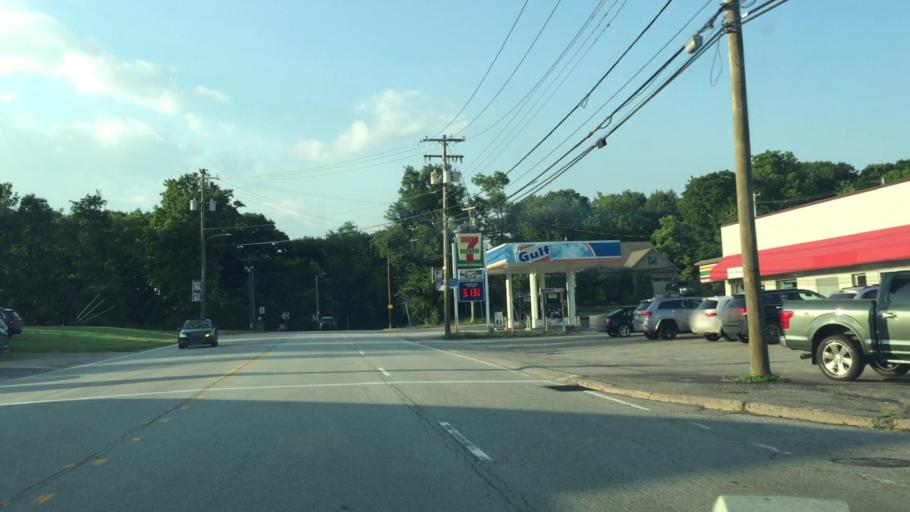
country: US
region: Pennsylvania
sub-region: Allegheny County
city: South Park Township
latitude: 40.3214
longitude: -79.9953
